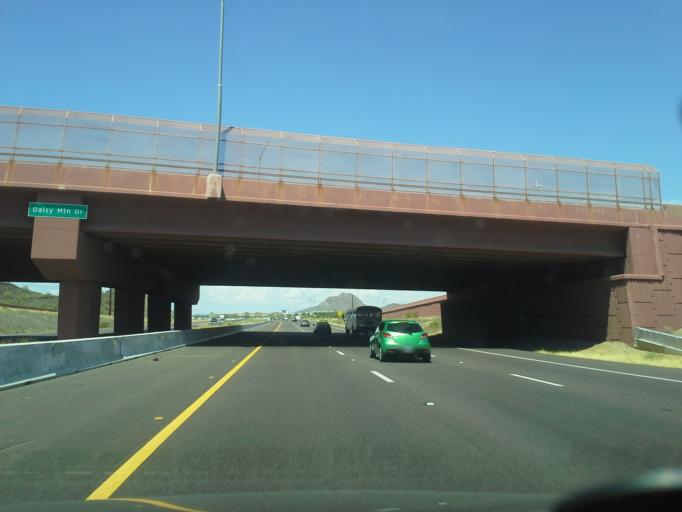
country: US
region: Arizona
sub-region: Maricopa County
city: Anthem
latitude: 33.8408
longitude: -112.1440
